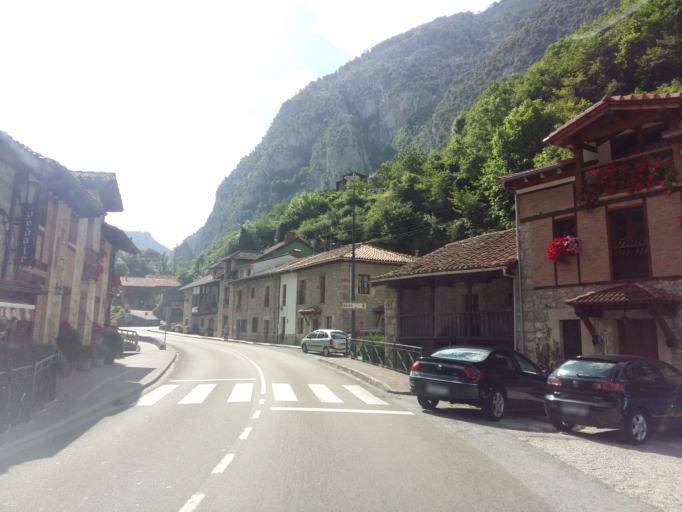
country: ES
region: Cantabria
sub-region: Provincia de Cantabria
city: Tresviso
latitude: 43.2548
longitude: -4.6151
